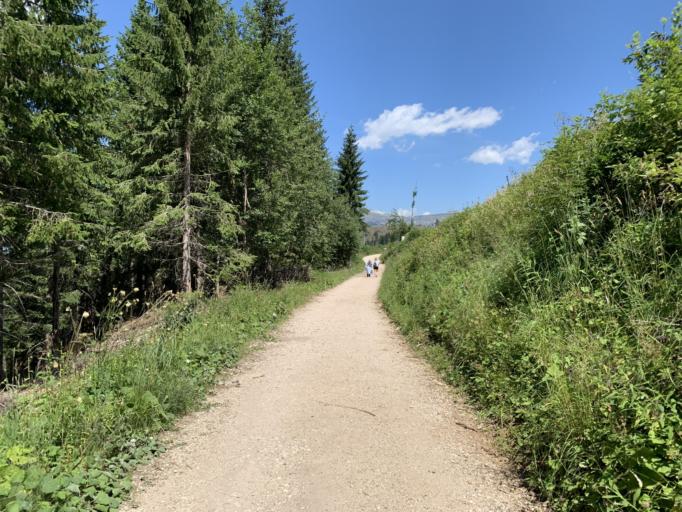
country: IT
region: Trentino-Alto Adige
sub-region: Bolzano
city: Nova Levante
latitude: 46.4057
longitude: 11.5810
